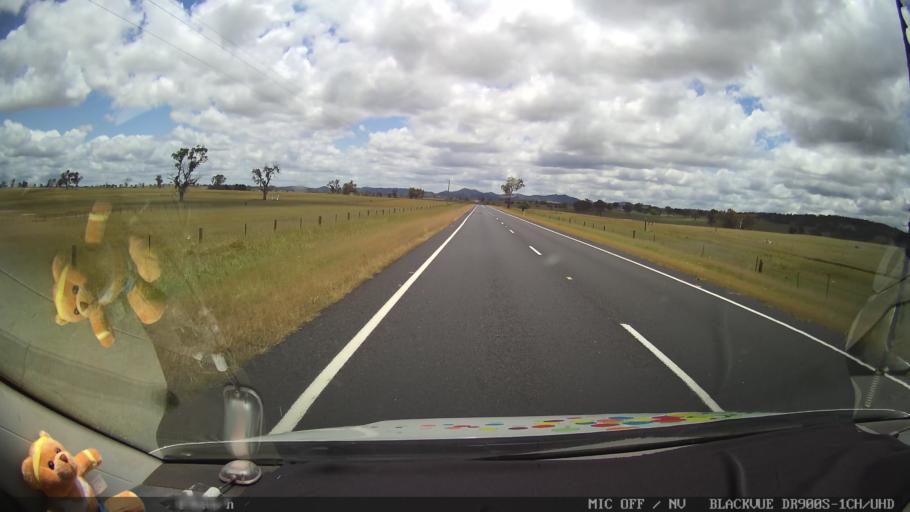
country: AU
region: New South Wales
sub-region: Glen Innes Severn
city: Glen Innes
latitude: -29.4259
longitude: 151.8582
